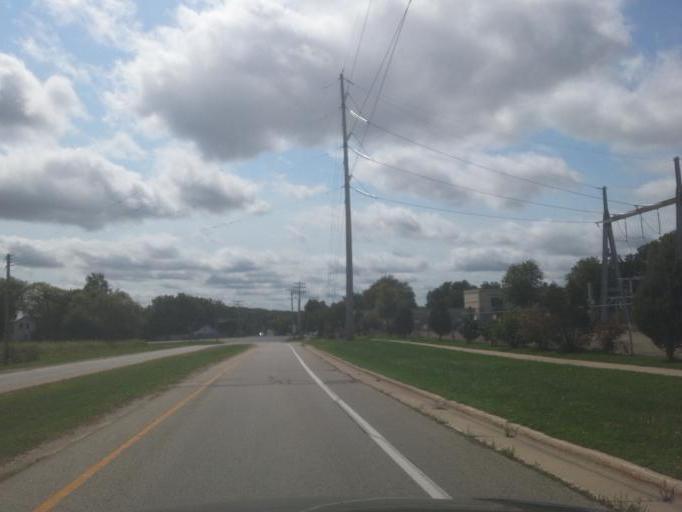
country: US
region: Wisconsin
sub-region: Dane County
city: Cottage Grove
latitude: 43.0867
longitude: -89.2668
